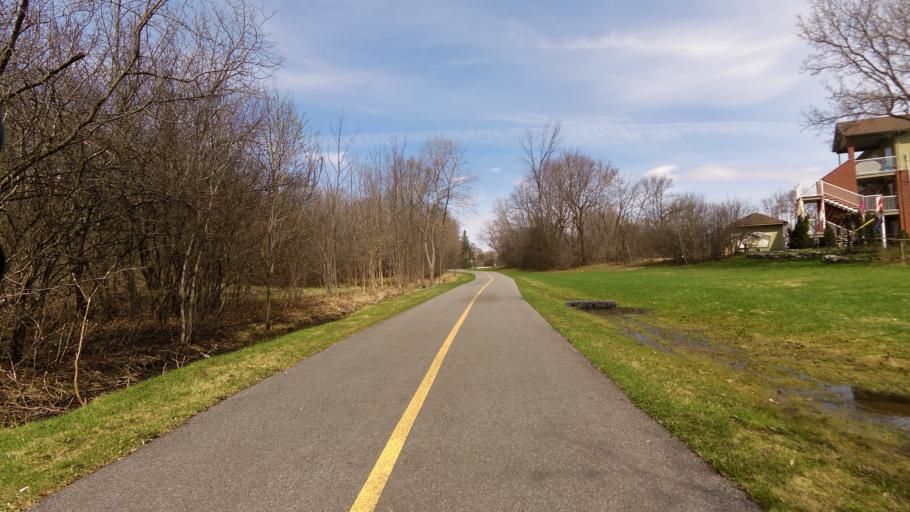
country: CA
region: Ontario
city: Ottawa
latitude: 45.4241
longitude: -75.7357
